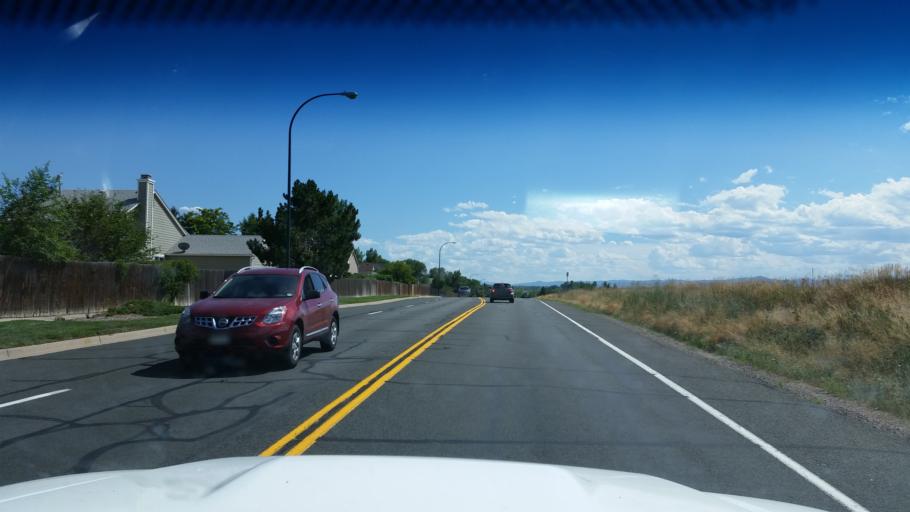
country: US
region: Colorado
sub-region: Broomfield County
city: Broomfield
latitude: 39.8836
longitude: -105.1287
